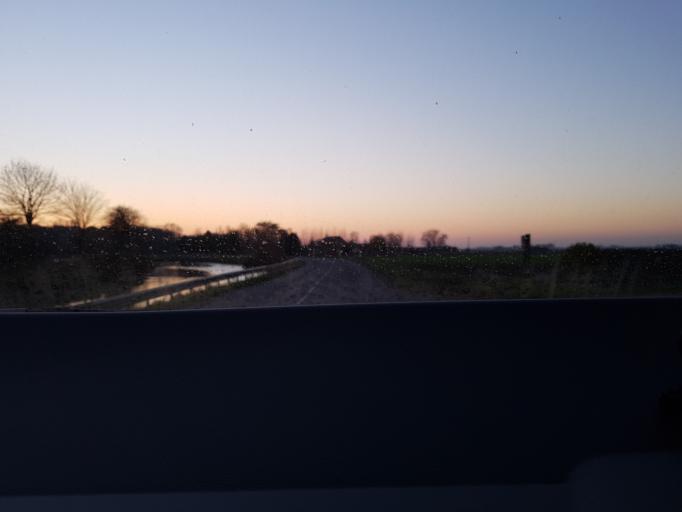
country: FR
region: Nord-Pas-de-Calais
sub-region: Departement du Nord
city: Spycker
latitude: 50.9595
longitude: 2.3248
